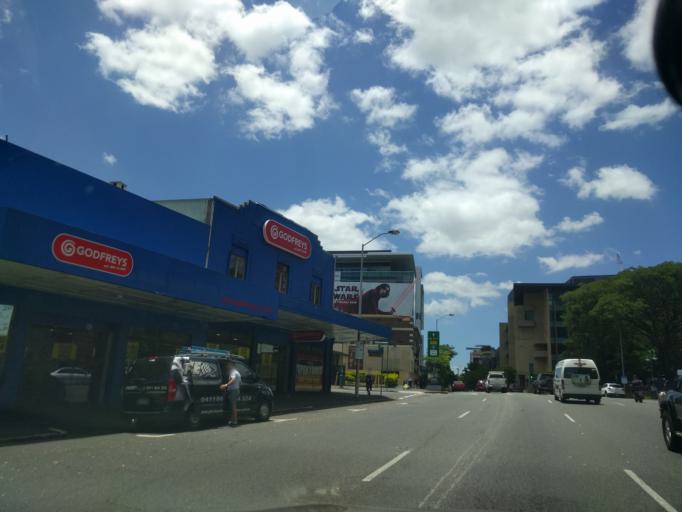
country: AU
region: Queensland
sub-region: Brisbane
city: Fortitude Valley
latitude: -27.4541
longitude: 153.0370
